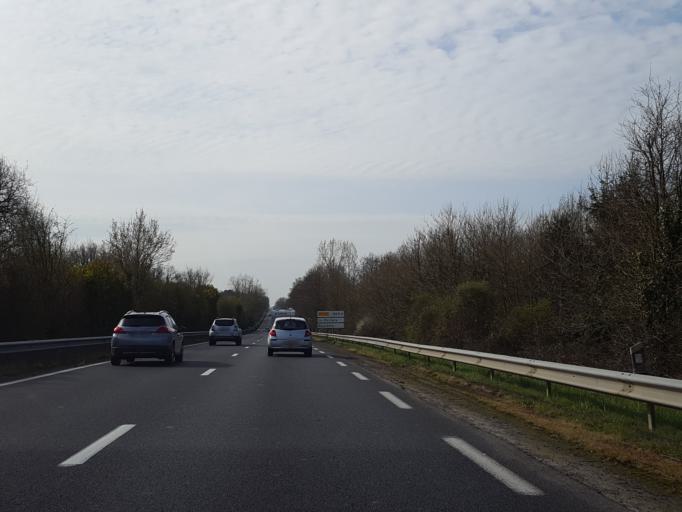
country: FR
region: Pays de la Loire
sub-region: Departement de la Vendee
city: Belleville-sur-Vie
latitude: 46.7660
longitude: -1.4310
